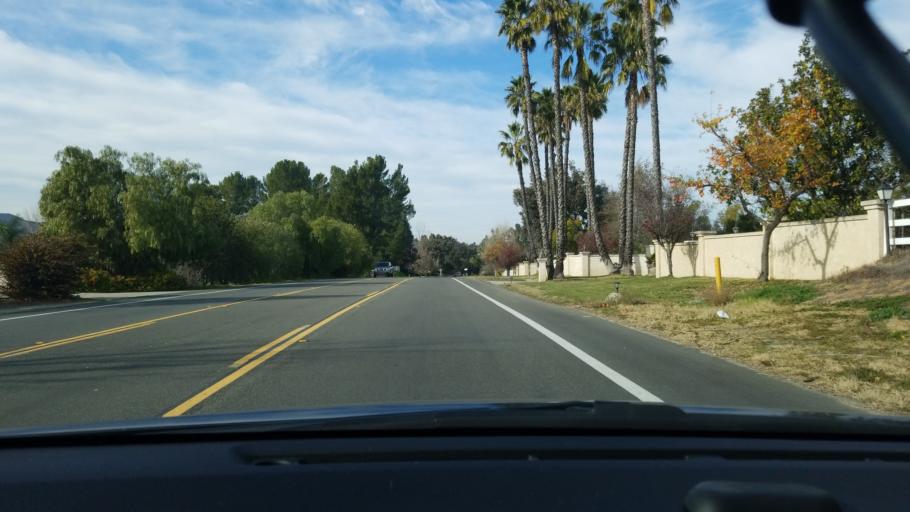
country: US
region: California
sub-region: Riverside County
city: Temecula
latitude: 33.4830
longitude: -117.1342
